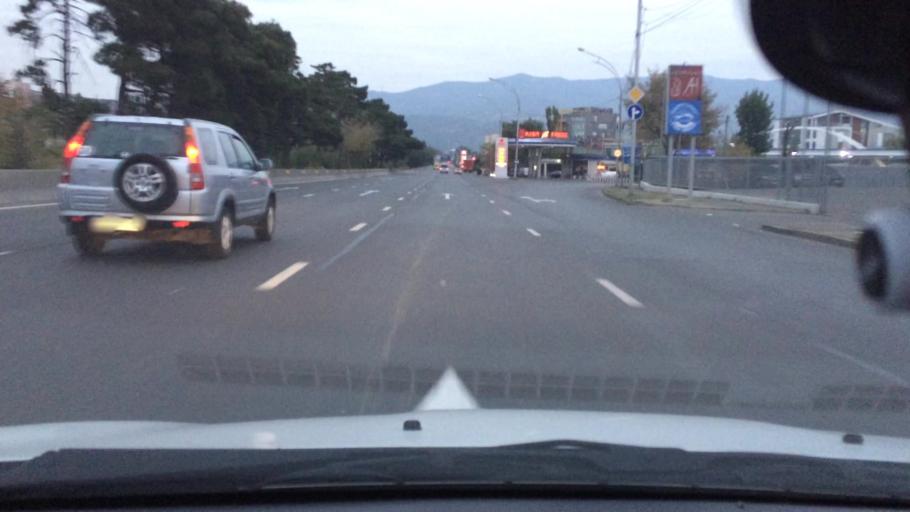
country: GE
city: Zahesi
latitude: 41.7853
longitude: 44.7700
